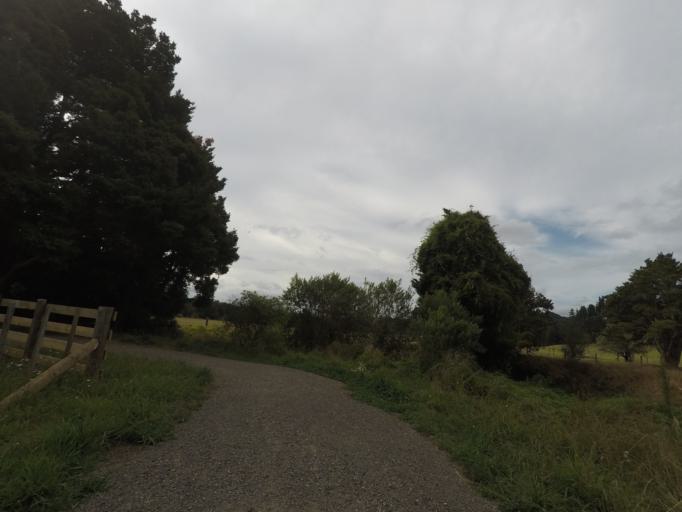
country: NZ
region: Northland
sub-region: Whangarei
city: Whangarei
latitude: -35.6770
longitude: 174.3344
